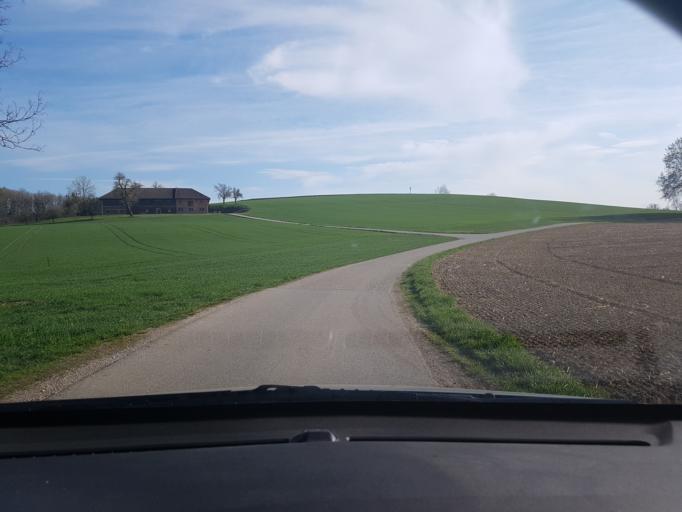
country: AT
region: Upper Austria
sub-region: Politischer Bezirk Linz-Land
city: Ansfelden
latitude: 48.1852
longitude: 14.3323
